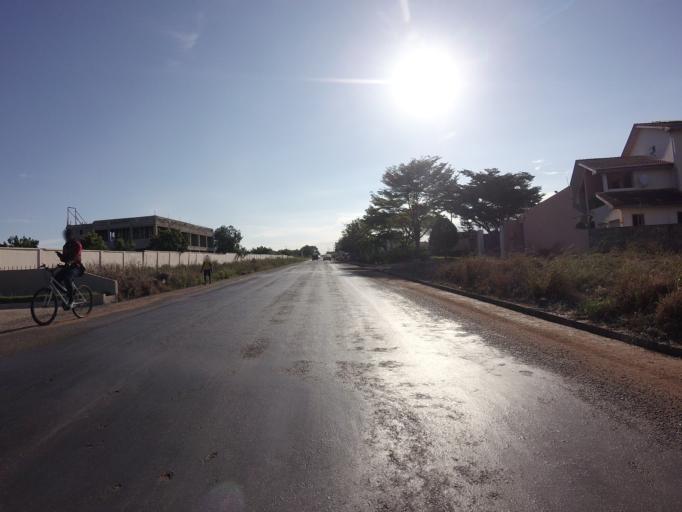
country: GH
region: Greater Accra
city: Nungua
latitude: 5.6515
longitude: -0.0688
